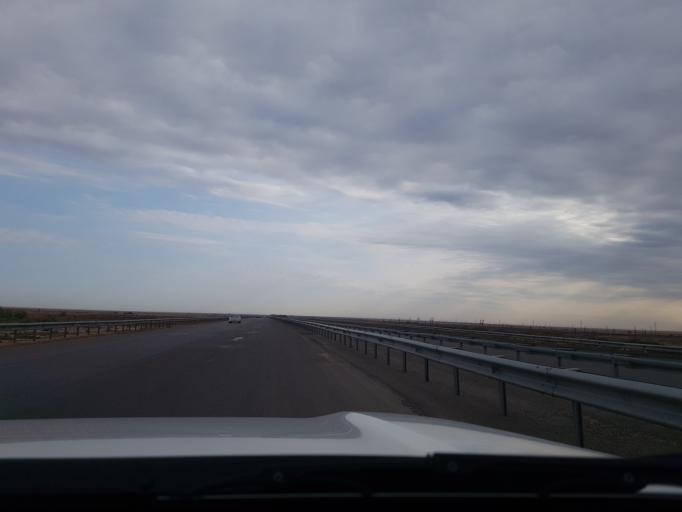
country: TM
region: Ahal
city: Tejen
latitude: 37.2333
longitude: 60.1537
